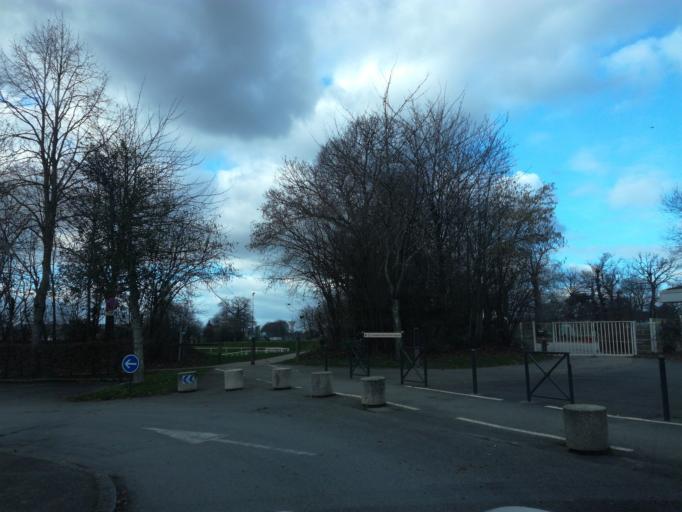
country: FR
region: Brittany
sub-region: Departement d'Ille-et-Vilaine
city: Fouillard
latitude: 48.1534
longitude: -1.5824
